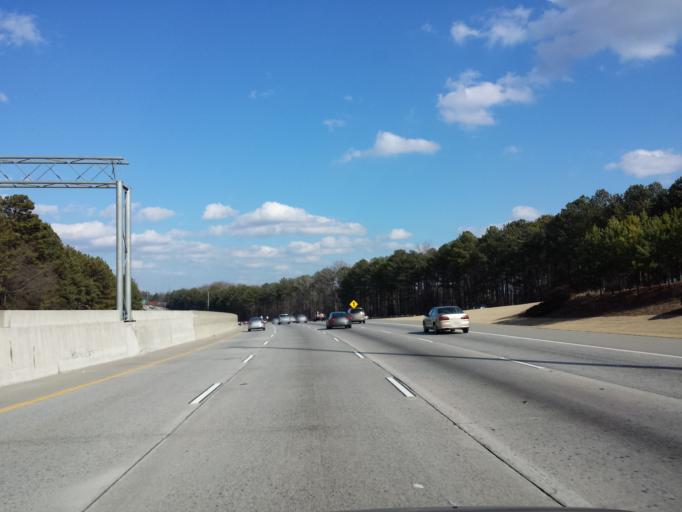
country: US
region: Georgia
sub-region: Fulton County
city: Alpharetta
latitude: 34.0545
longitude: -84.2853
